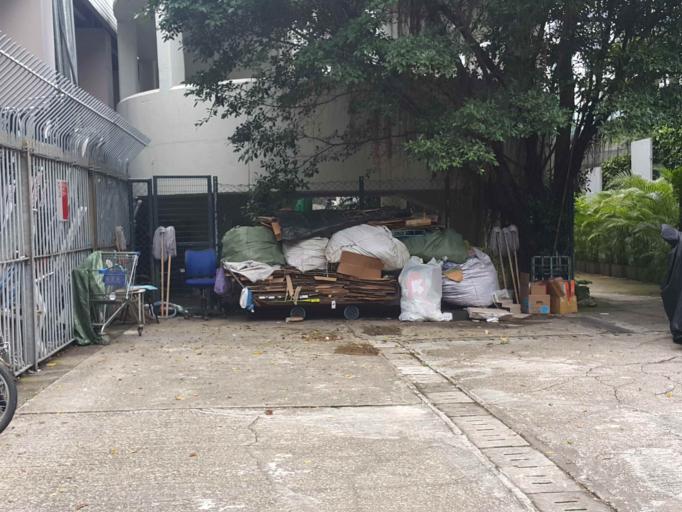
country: HK
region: Wong Tai Sin
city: Wong Tai Sin
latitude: 22.3377
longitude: 114.1751
